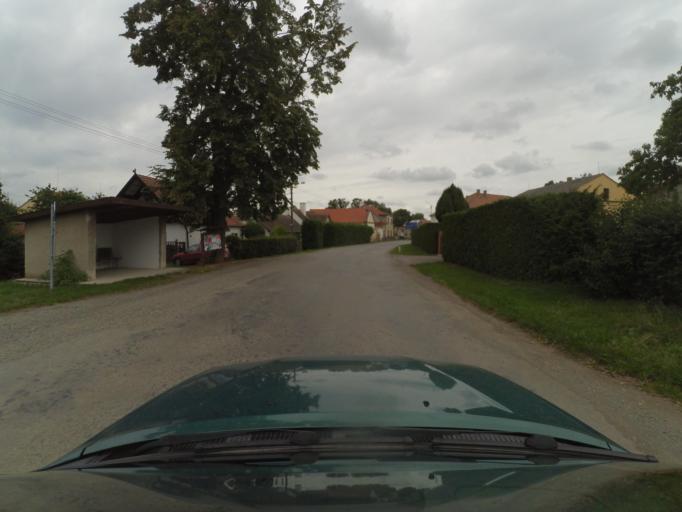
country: CZ
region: Plzensky
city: Kozlany
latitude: 49.9706
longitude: 13.5395
